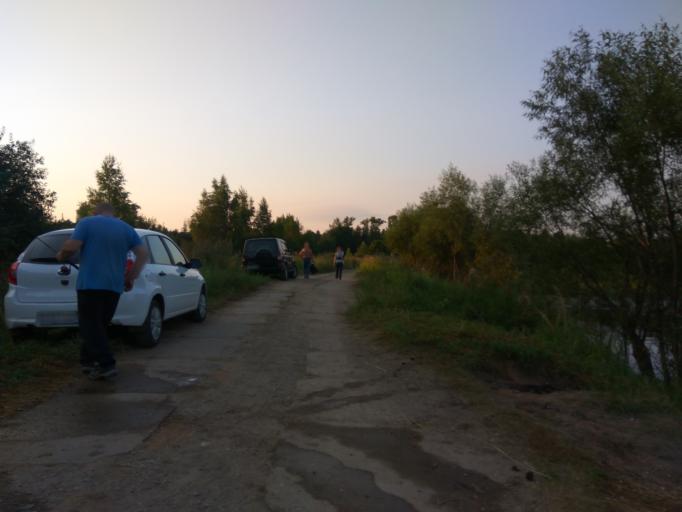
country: RU
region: Moskovskaya
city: Kubinka
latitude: 55.5856
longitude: 36.7408
